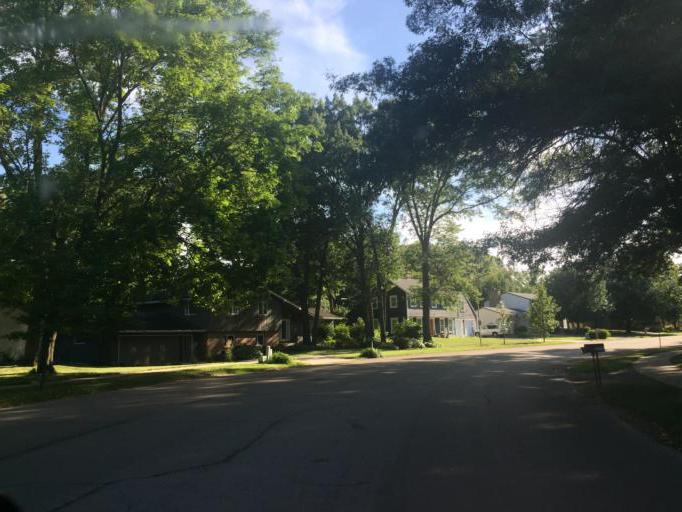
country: US
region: Minnesota
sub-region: Olmsted County
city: Rochester
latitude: 44.0143
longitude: -92.4901
